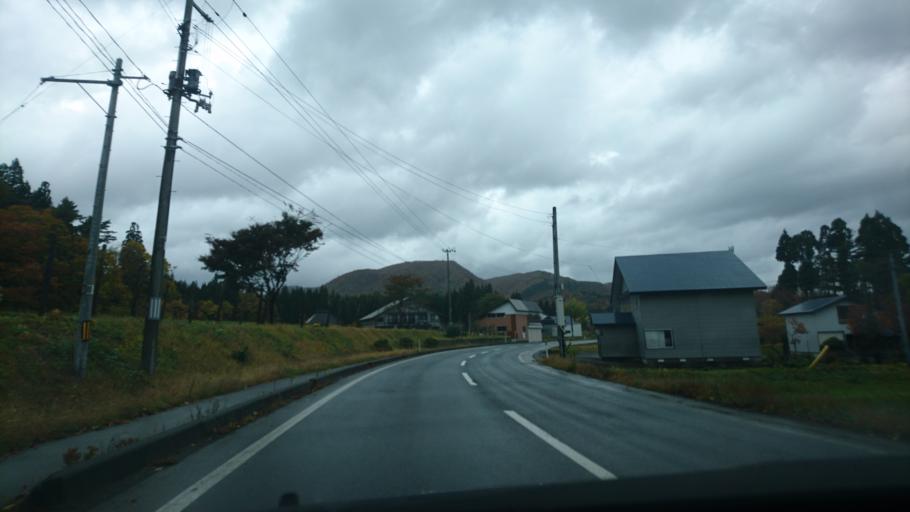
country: JP
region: Akita
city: Kakunodatemachi
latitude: 39.4719
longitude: 140.7817
